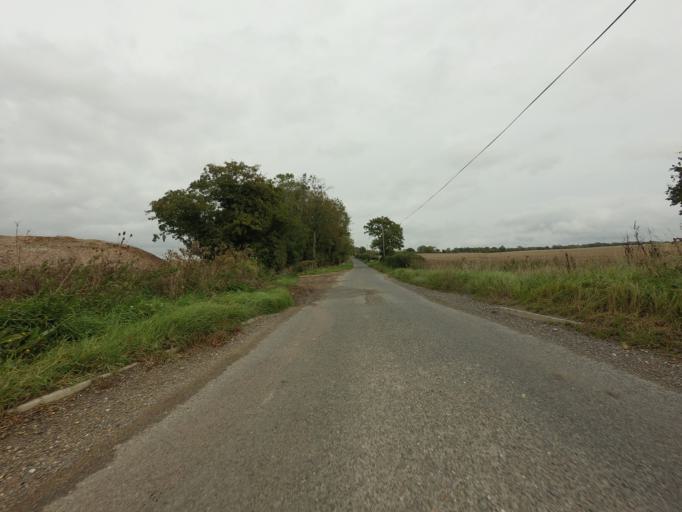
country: GB
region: England
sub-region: Cambridgeshire
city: Duxford
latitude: 52.0182
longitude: 0.1516
